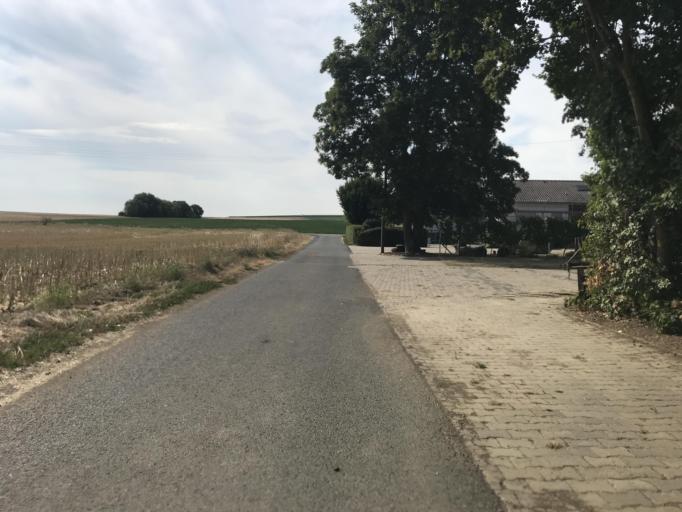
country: DE
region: Rheinland-Pfalz
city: Bechtolsheim
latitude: 49.8102
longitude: 8.2059
